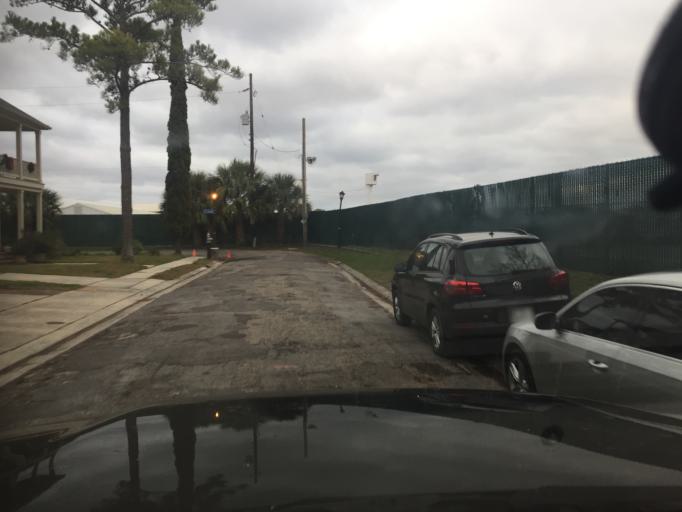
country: US
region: Louisiana
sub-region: Orleans Parish
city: New Orleans
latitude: 29.9836
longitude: -90.0853
